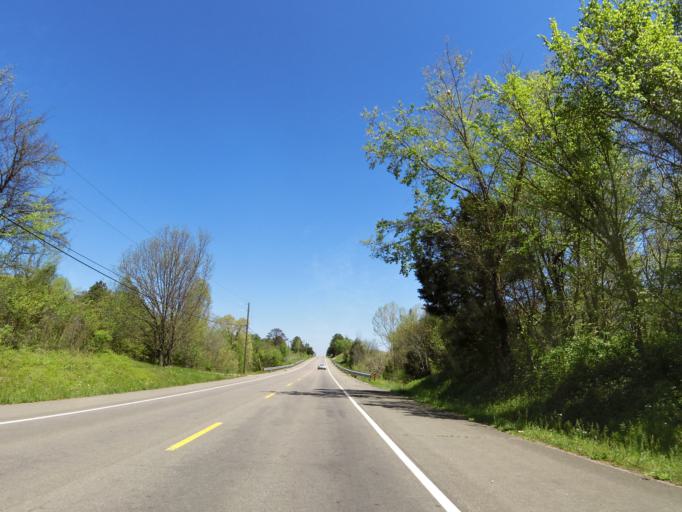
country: US
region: Tennessee
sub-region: Greene County
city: Mosheim
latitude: 36.0536
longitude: -82.9838
